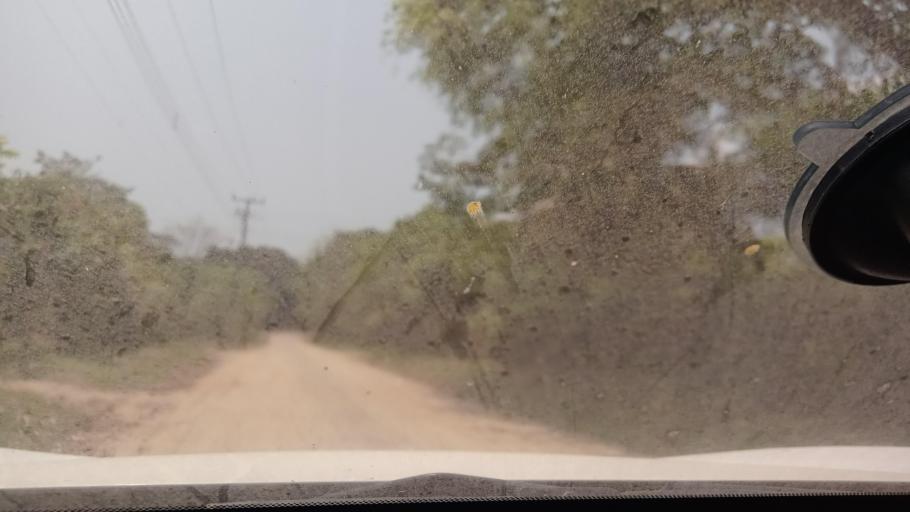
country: MX
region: Chiapas
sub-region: Tecpatan
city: Raudales Malpaso
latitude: 17.4562
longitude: -93.7969
